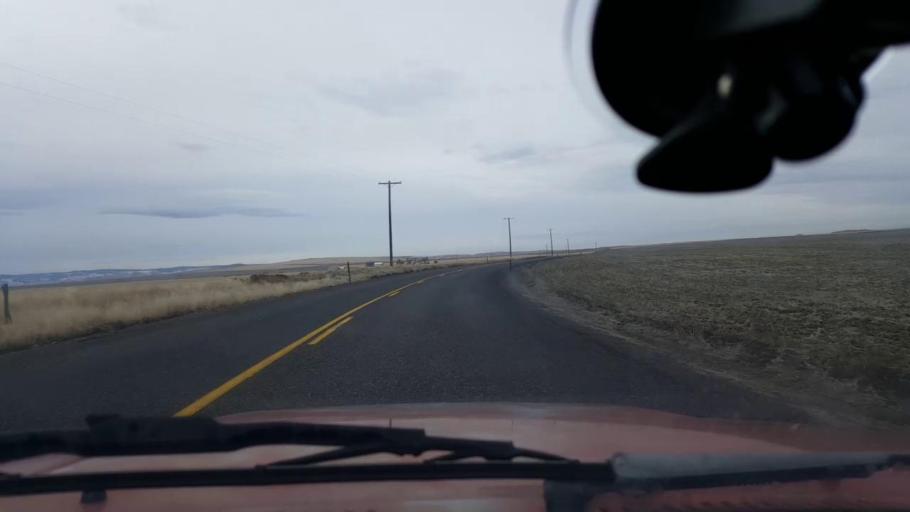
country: US
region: Washington
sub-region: Asotin County
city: Clarkston Heights-Vineland
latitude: 46.3750
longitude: -117.1582
